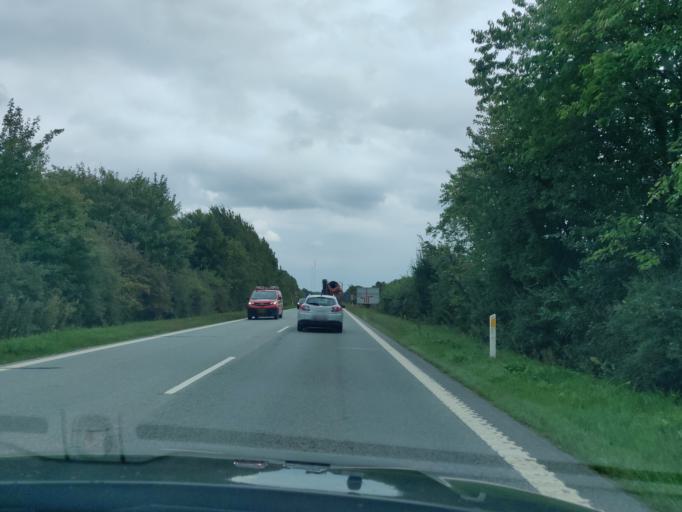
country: DK
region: North Denmark
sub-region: Alborg Kommune
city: Frejlev
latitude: 57.0119
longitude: 9.7668
